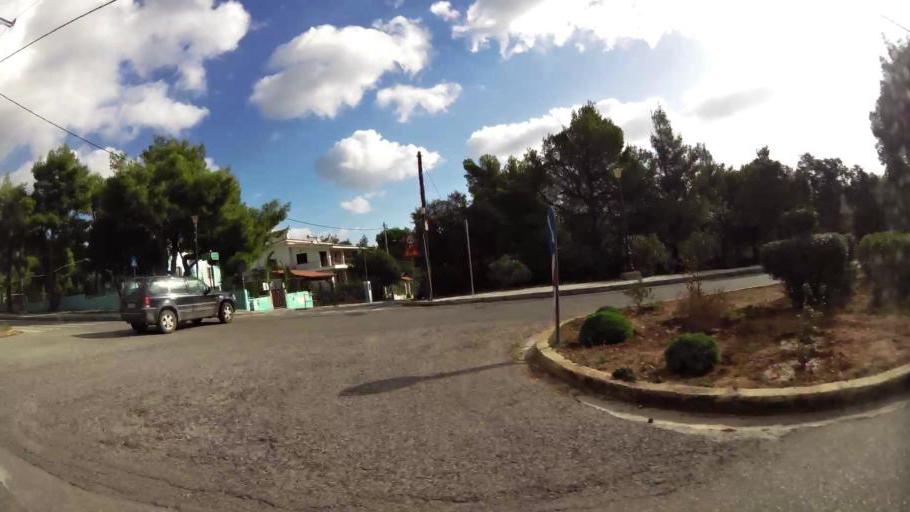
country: GR
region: Attica
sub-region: Nomarchia Anatolikis Attikis
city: Thrakomakedones
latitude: 38.1335
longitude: 23.7568
